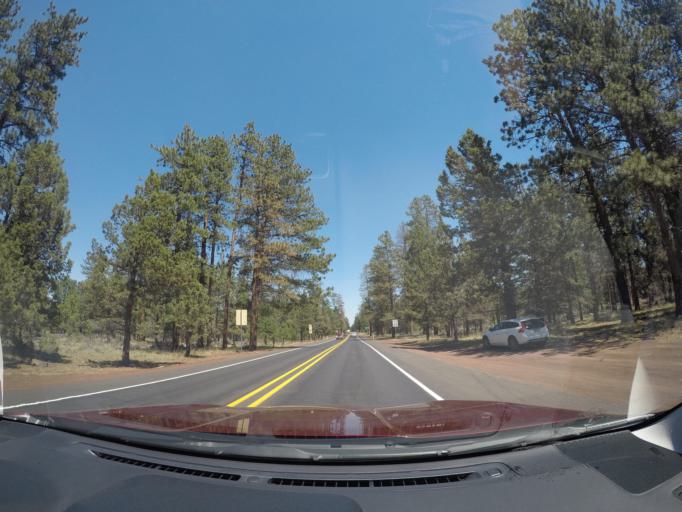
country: US
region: Oregon
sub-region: Deschutes County
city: Sisters
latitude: 44.2877
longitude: -121.5386
